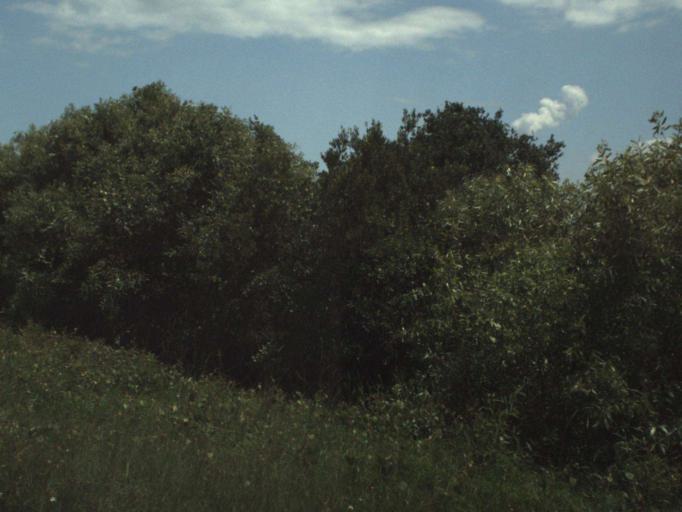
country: US
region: Florida
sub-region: Brevard County
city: Merritt Island
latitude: 28.6435
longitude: -80.6677
